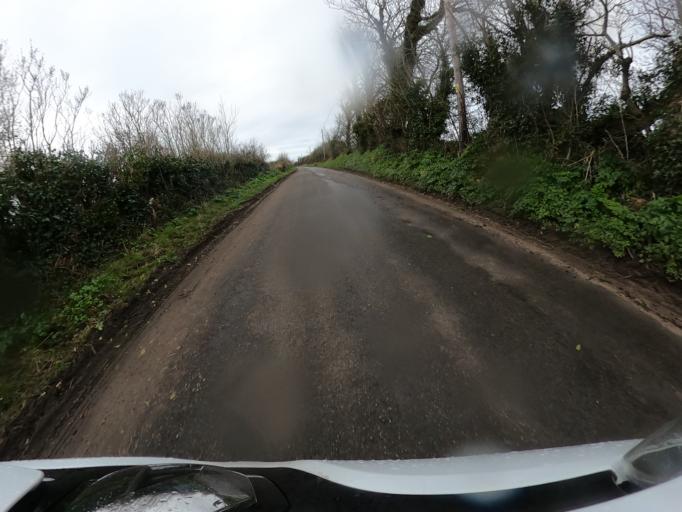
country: IM
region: Ramsey
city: Ramsey
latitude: 54.3780
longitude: -4.4541
